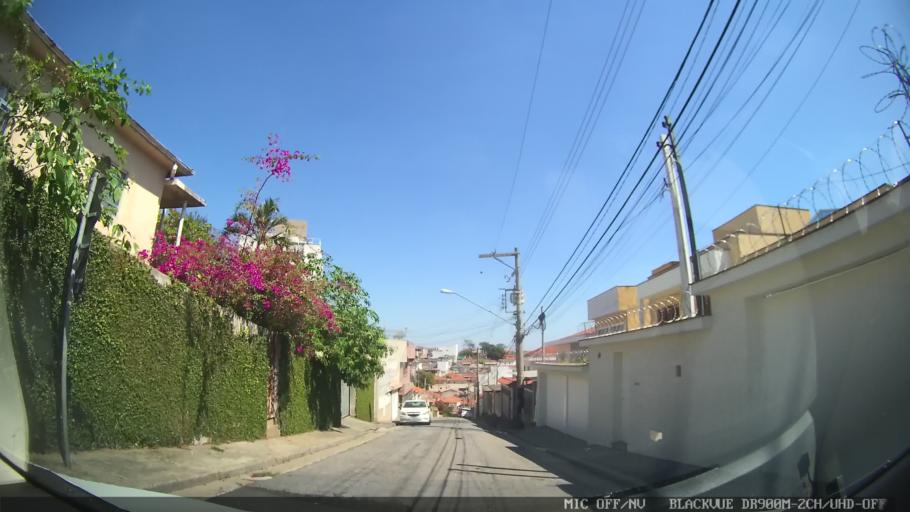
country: BR
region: Sao Paulo
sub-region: Sao Paulo
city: Sao Paulo
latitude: -23.4934
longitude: -46.6502
